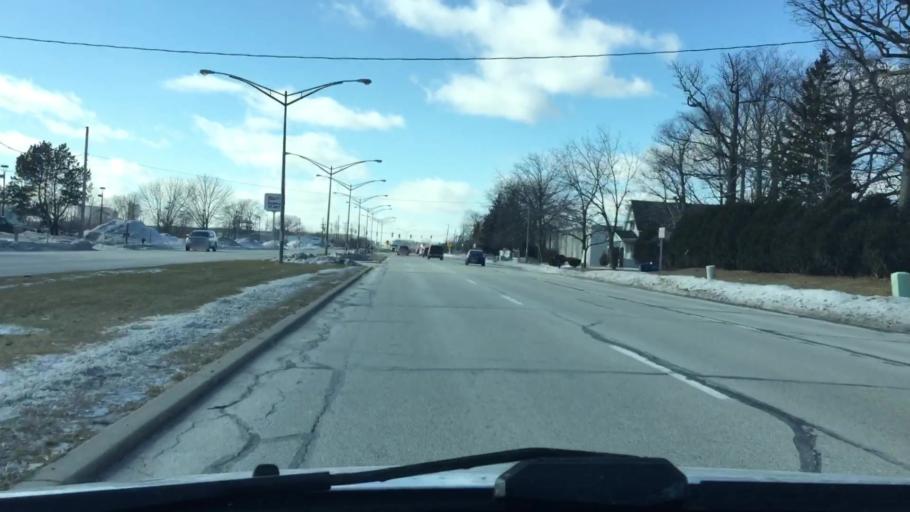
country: US
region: Wisconsin
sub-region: Milwaukee County
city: South Milwaukee
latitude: 42.9158
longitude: -87.9157
